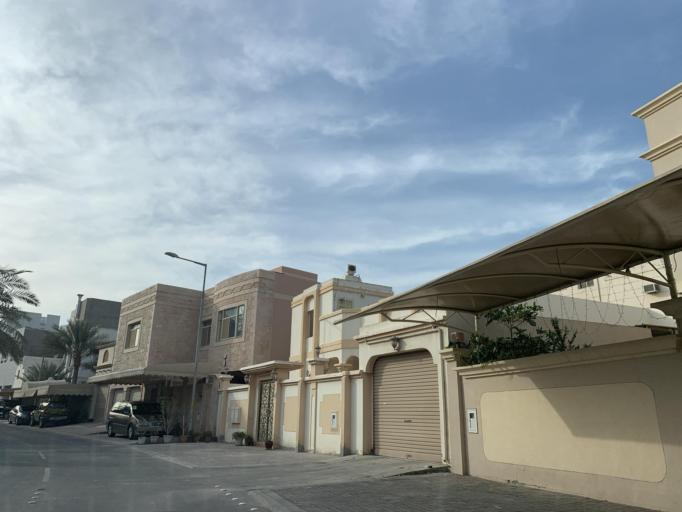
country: BH
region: Northern
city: Ar Rifa'
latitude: 26.1255
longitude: 50.5836
